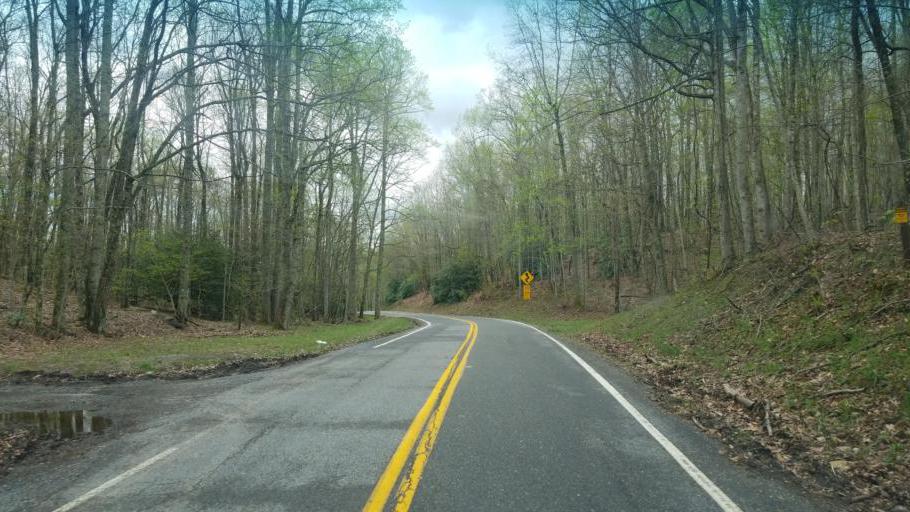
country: US
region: Virginia
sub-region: Tazewell County
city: Tazewell
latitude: 36.9963
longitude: -81.5339
